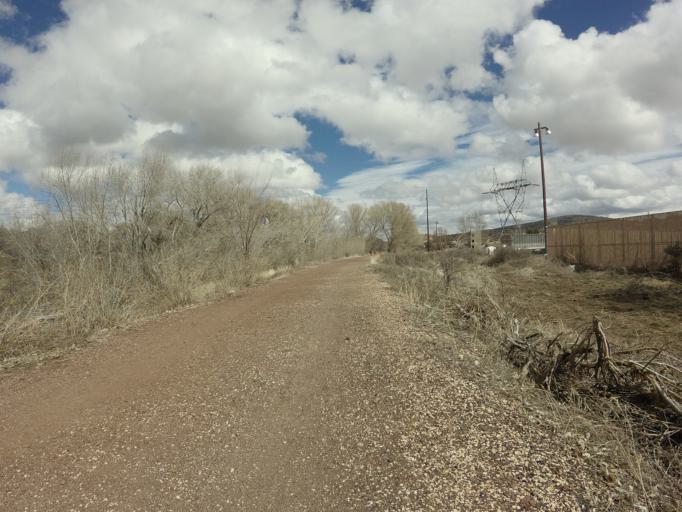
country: US
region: Arizona
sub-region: Yavapai County
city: Prescott
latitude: 34.5796
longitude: -112.4256
